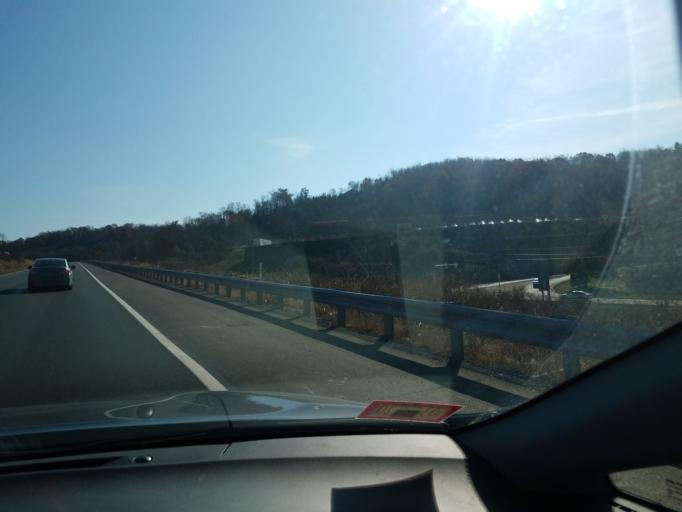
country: US
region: Pennsylvania
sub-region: Allegheny County
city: Ben Avon
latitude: 40.5239
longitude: -80.0701
